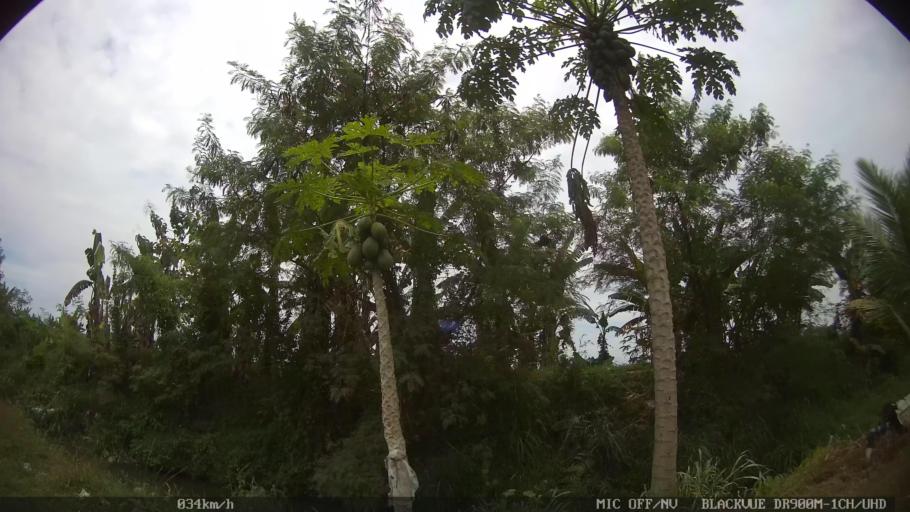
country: ID
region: North Sumatra
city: Sunggal
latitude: 3.6351
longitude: 98.5734
